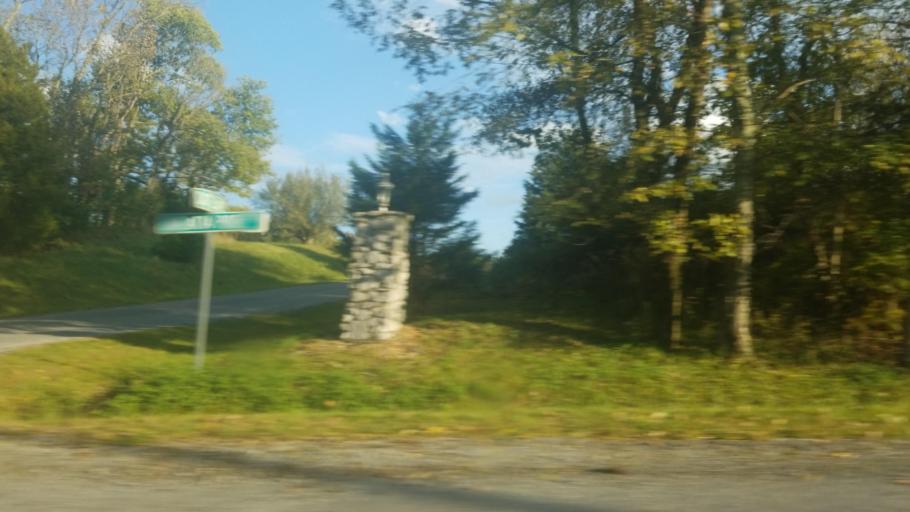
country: US
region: Illinois
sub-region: Williamson County
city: Marion
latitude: 37.7635
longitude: -88.7790
